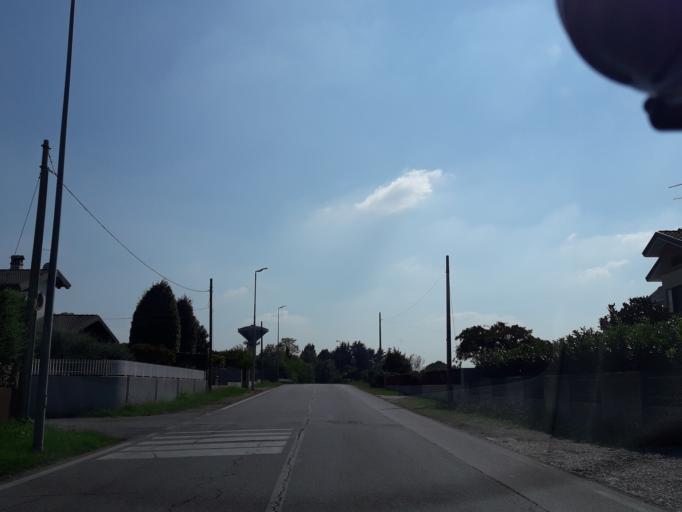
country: IT
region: Friuli Venezia Giulia
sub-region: Provincia di Udine
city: Tavagnacco
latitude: 46.1124
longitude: 13.2105
